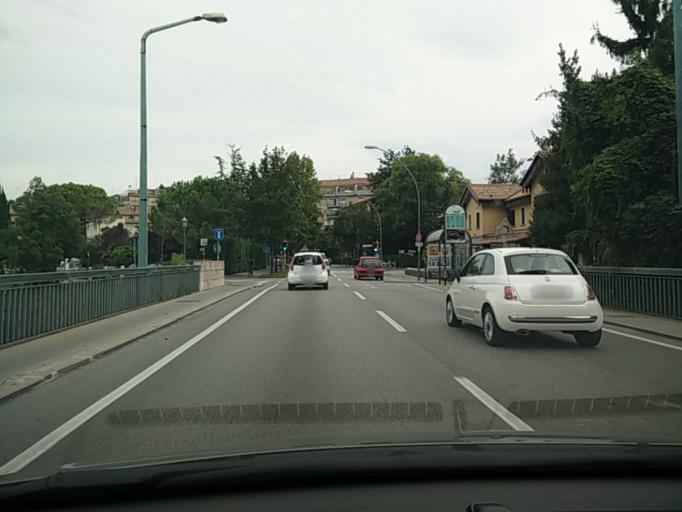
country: IT
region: Veneto
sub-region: Provincia di Treviso
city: Treviso
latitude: 45.6617
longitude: 12.2378
